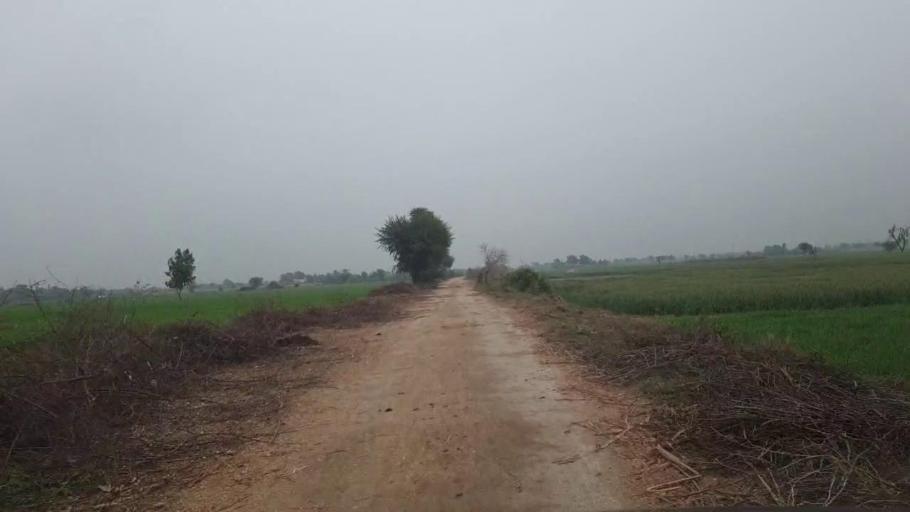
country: PK
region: Sindh
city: Tando Adam
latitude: 25.8461
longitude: 68.7040
